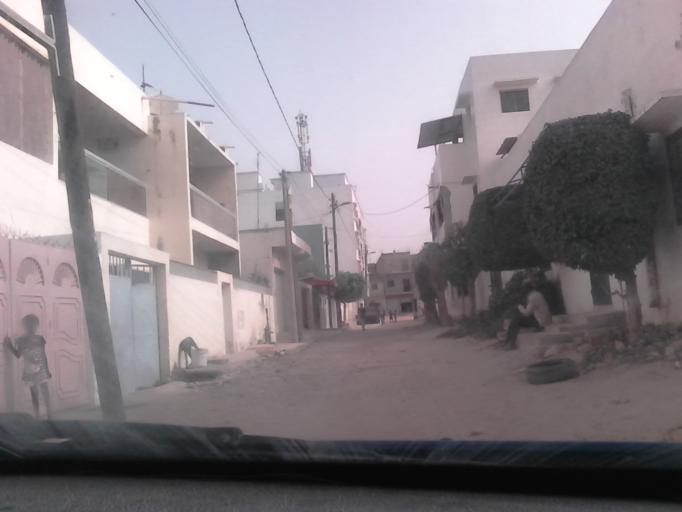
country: SN
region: Dakar
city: Grand Dakar
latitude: 14.7034
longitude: -17.4522
